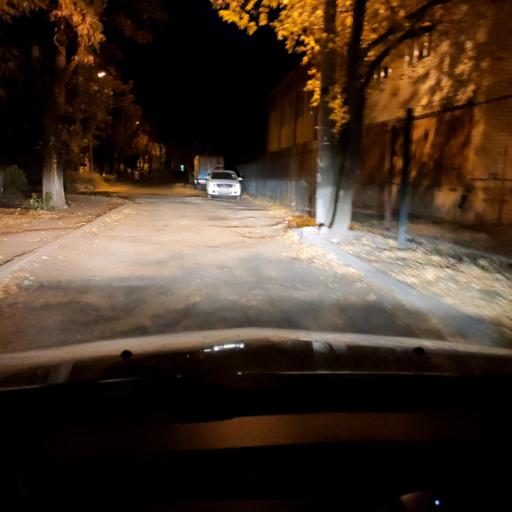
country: RU
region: Voronezj
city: Voronezh
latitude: 51.6540
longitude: 39.1554
